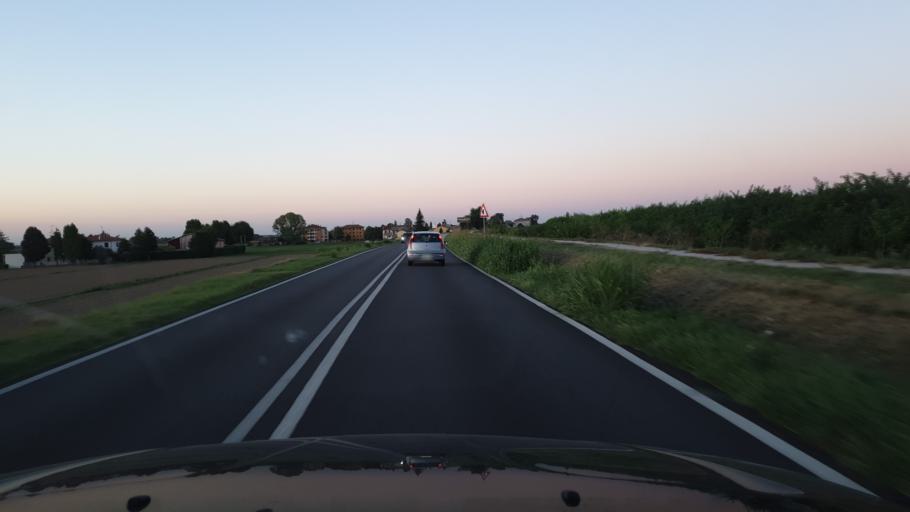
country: IT
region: Emilia-Romagna
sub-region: Provincia di Bologna
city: Ca De Fabbri
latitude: 44.6231
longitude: 11.4566
